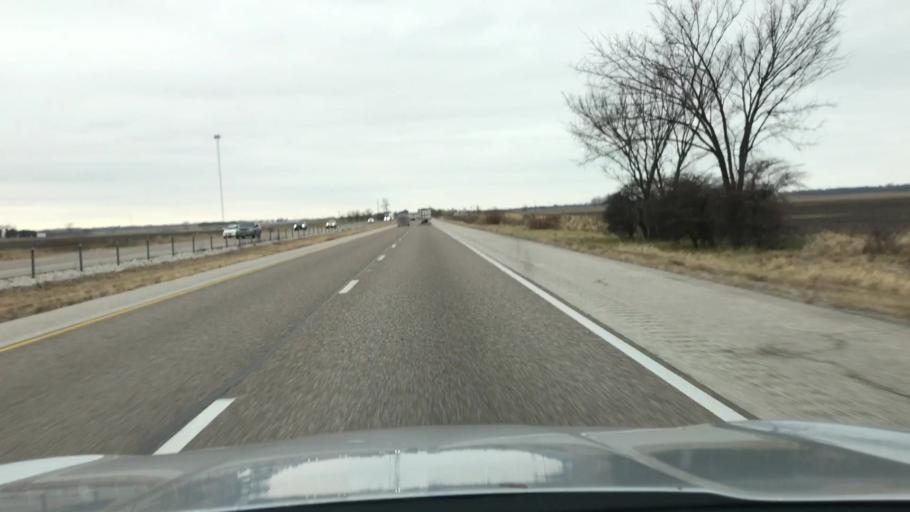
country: US
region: Illinois
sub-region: Madison County
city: Edwardsville
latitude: 38.8394
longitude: -89.8732
